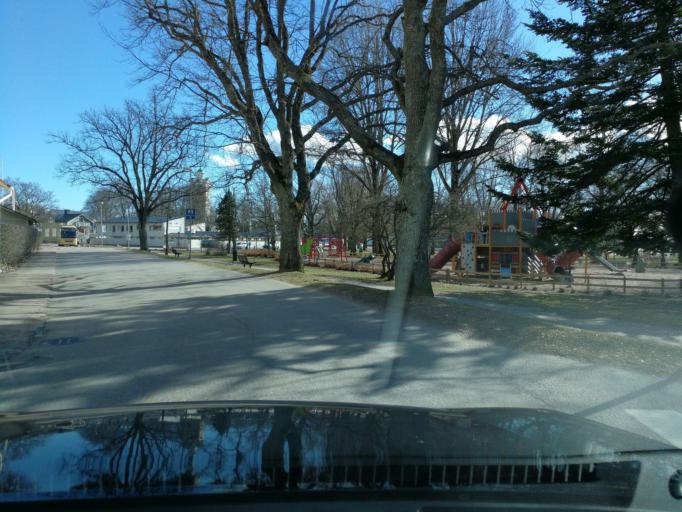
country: FI
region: Uusimaa
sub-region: Raaseporin
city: Ekenaes
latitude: 59.9765
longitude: 23.4326
